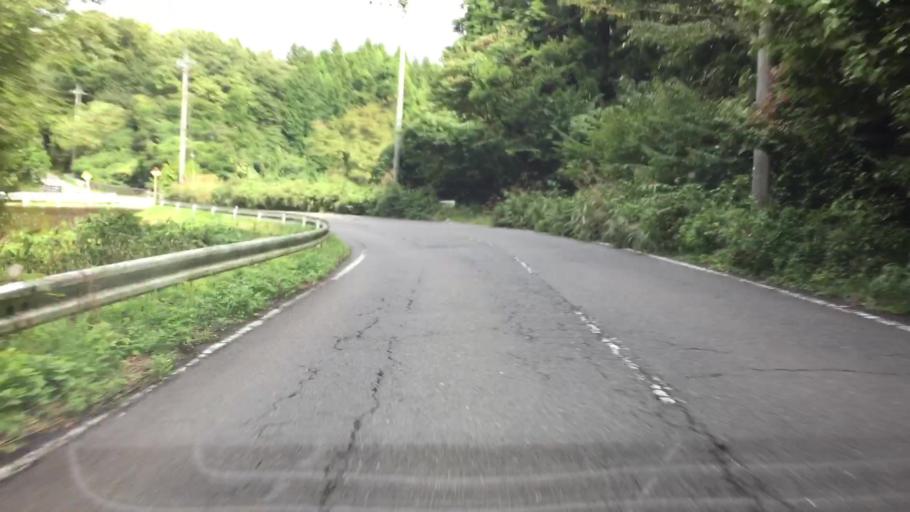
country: JP
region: Tochigi
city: Imaichi
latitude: 36.7552
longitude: 139.6640
